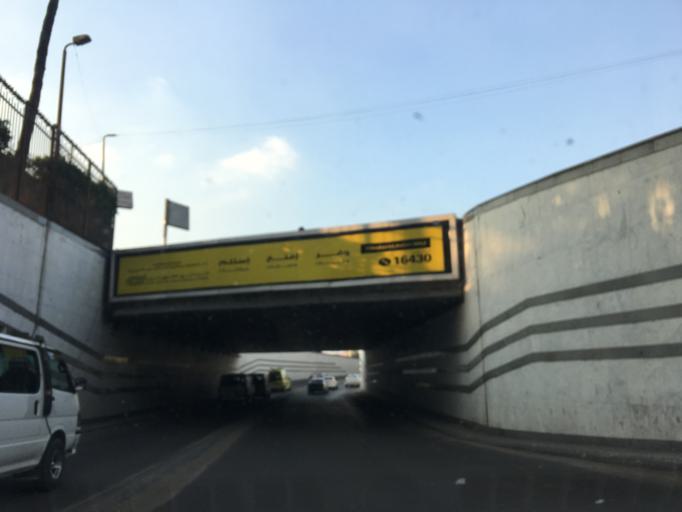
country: EG
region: Muhafazat al Qahirah
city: Cairo
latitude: 30.0438
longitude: 31.2322
